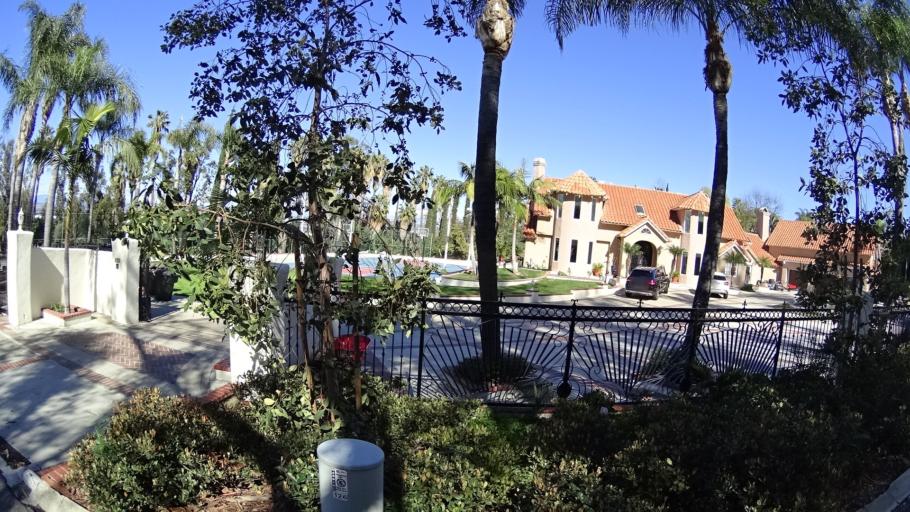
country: US
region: California
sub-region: Orange County
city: Villa Park
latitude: 33.8428
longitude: -117.8263
